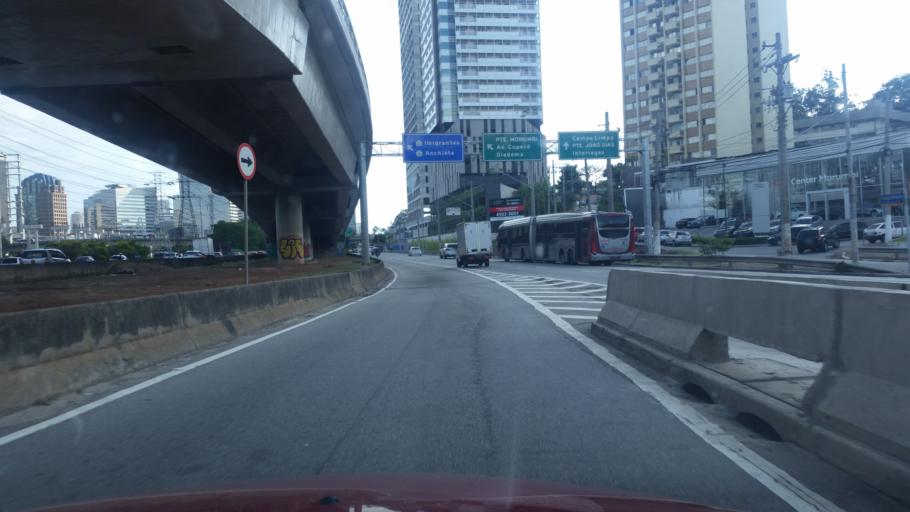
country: BR
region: Sao Paulo
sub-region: Taboao Da Serra
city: Taboao da Serra
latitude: -23.6141
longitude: -46.7010
